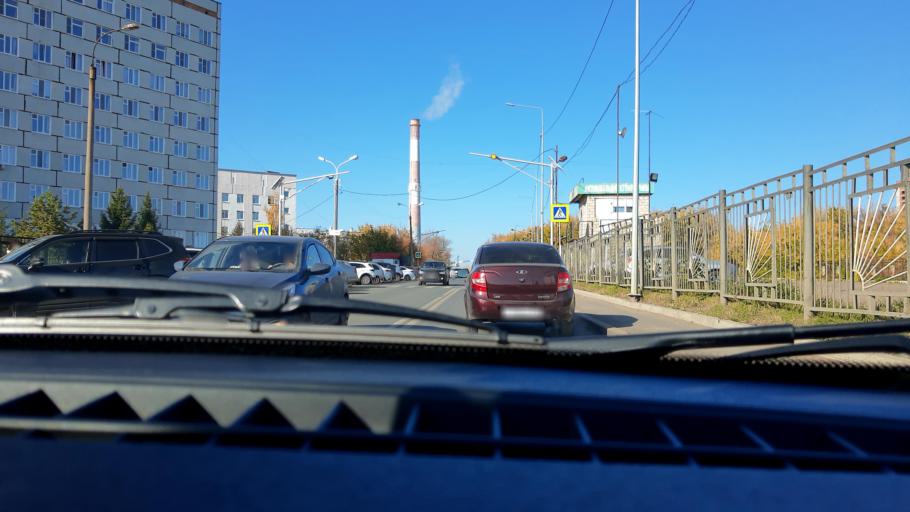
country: RU
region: Bashkortostan
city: Ufa
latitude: 54.7102
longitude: 56.0091
